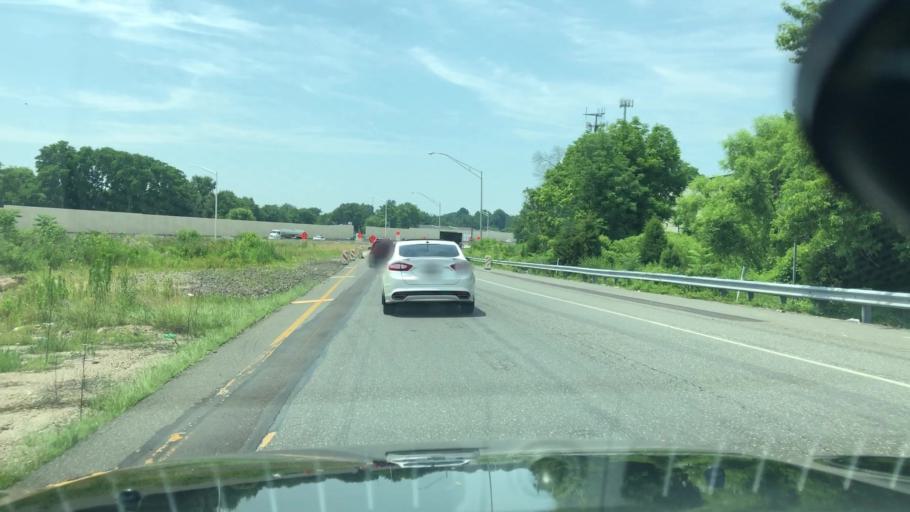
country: US
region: Pennsylvania
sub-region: Bucks County
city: Croydon
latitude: 40.1079
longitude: -74.8952
